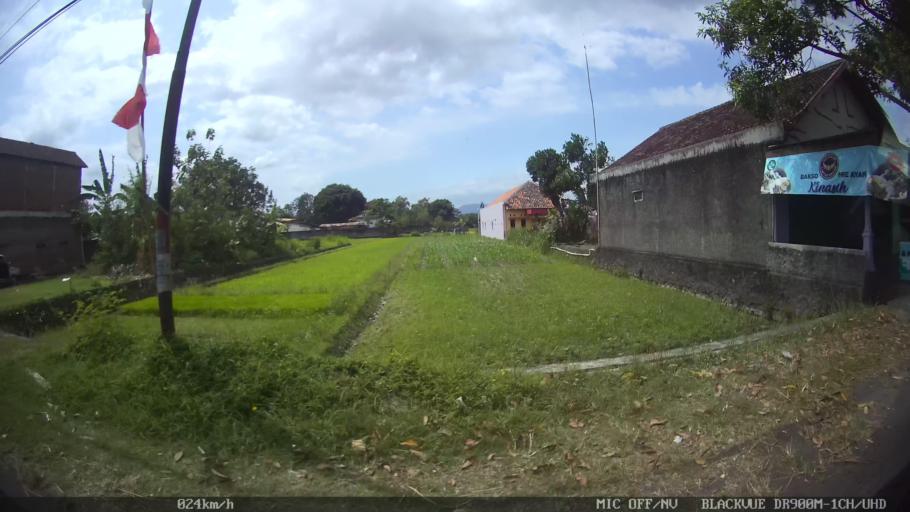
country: ID
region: Daerah Istimewa Yogyakarta
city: Depok
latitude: -7.7958
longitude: 110.4568
